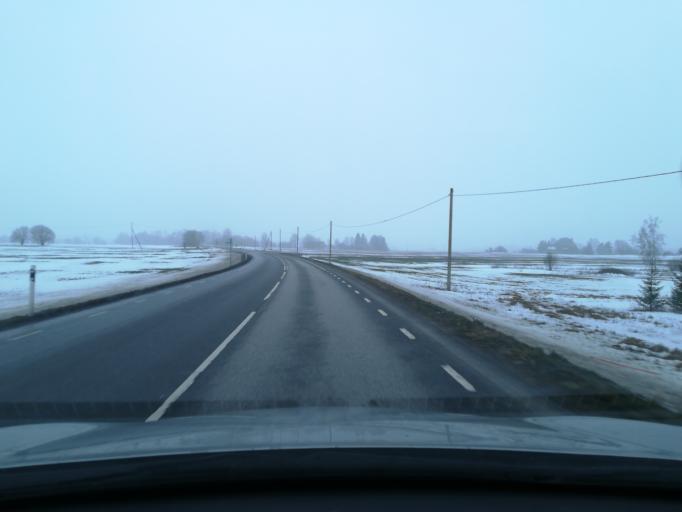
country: EE
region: Harju
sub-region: Raasiku vald
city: Raasiku
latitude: 59.3546
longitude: 25.1457
